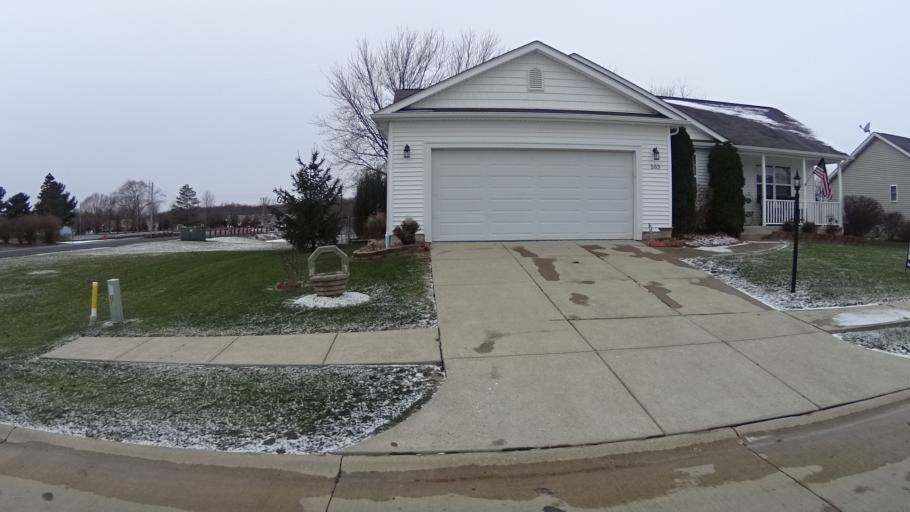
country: US
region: Ohio
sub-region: Lorain County
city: Lagrange
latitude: 41.2078
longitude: -82.1564
